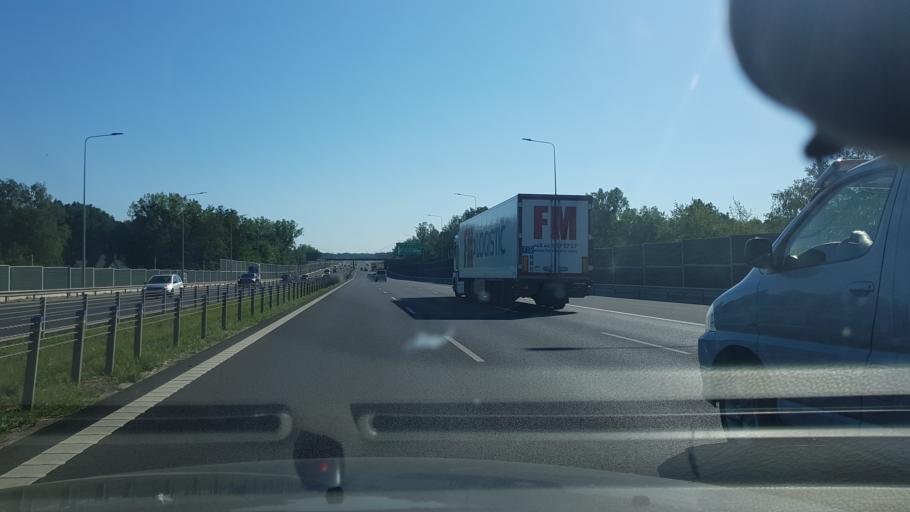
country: PL
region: Masovian Voivodeship
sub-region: Powiat wolominski
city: Marki
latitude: 52.3144
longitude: 21.1300
